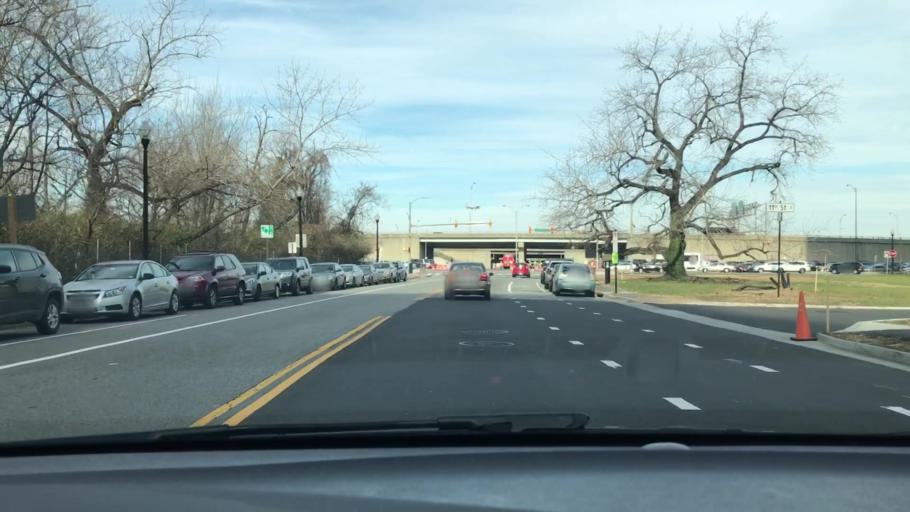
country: US
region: Washington, D.C.
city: Washington, D.C.
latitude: 38.8637
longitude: -77.0544
